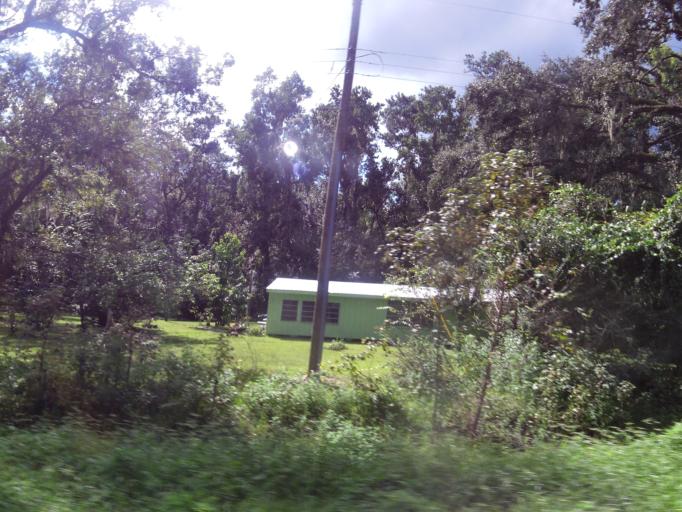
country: US
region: Florida
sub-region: Putnam County
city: East Palatka
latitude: 29.7435
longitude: -81.4756
